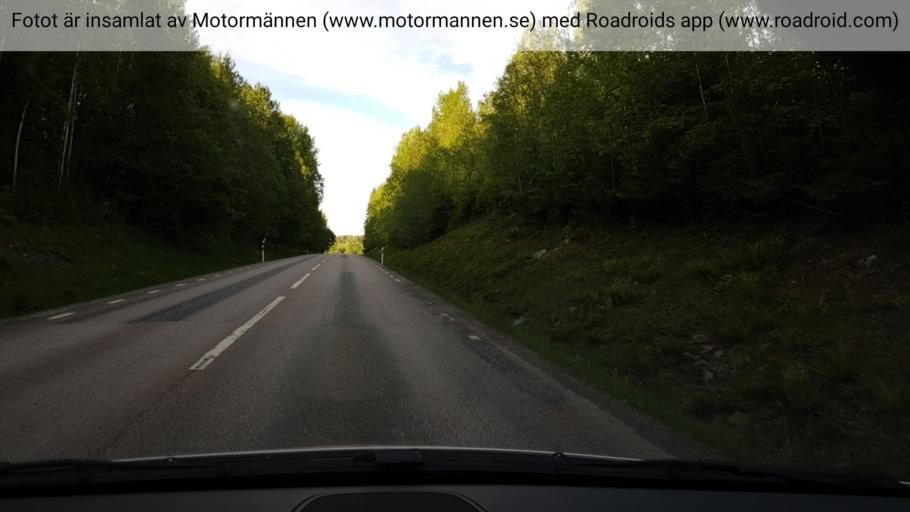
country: SE
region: Vaestmanland
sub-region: Skinnskattebergs Kommun
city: Skinnskatteberg
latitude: 59.8745
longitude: 15.6526
